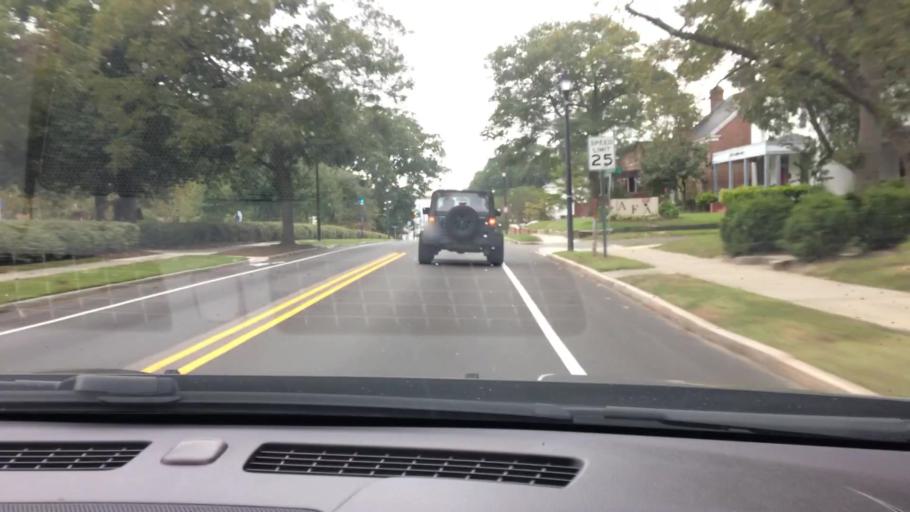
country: US
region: North Carolina
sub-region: Pitt County
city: Greenville
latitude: 35.6098
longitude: -77.3679
